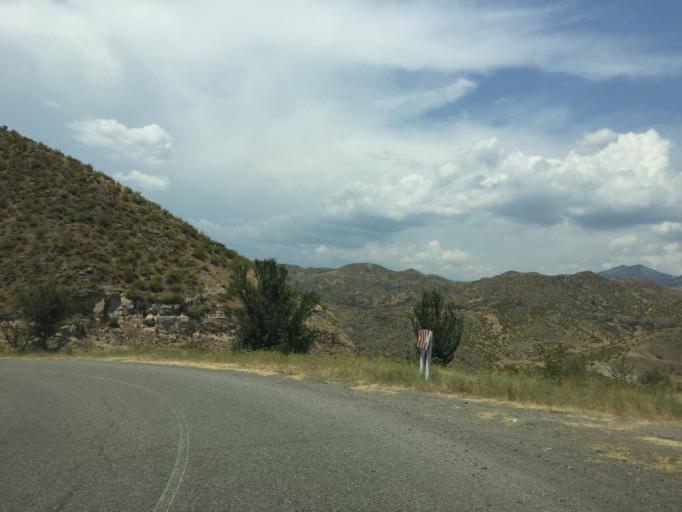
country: AZ
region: Lacin
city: Lacin
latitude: 39.5871
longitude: 46.5397
